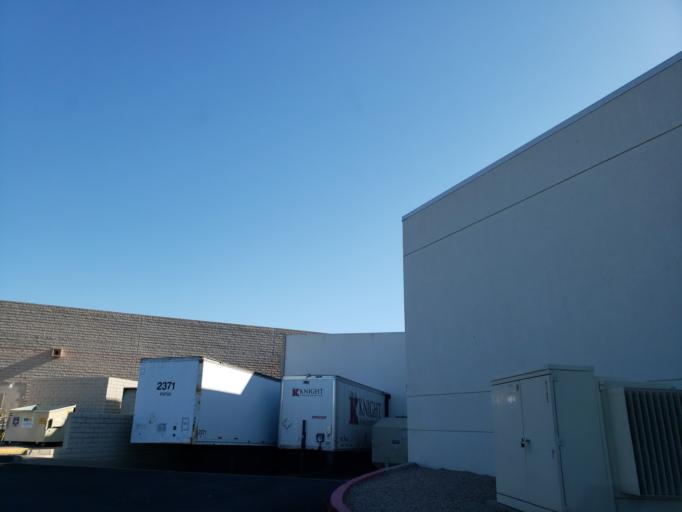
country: US
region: Arizona
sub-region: Maricopa County
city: Paradise Valley
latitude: 33.6015
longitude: -111.9844
